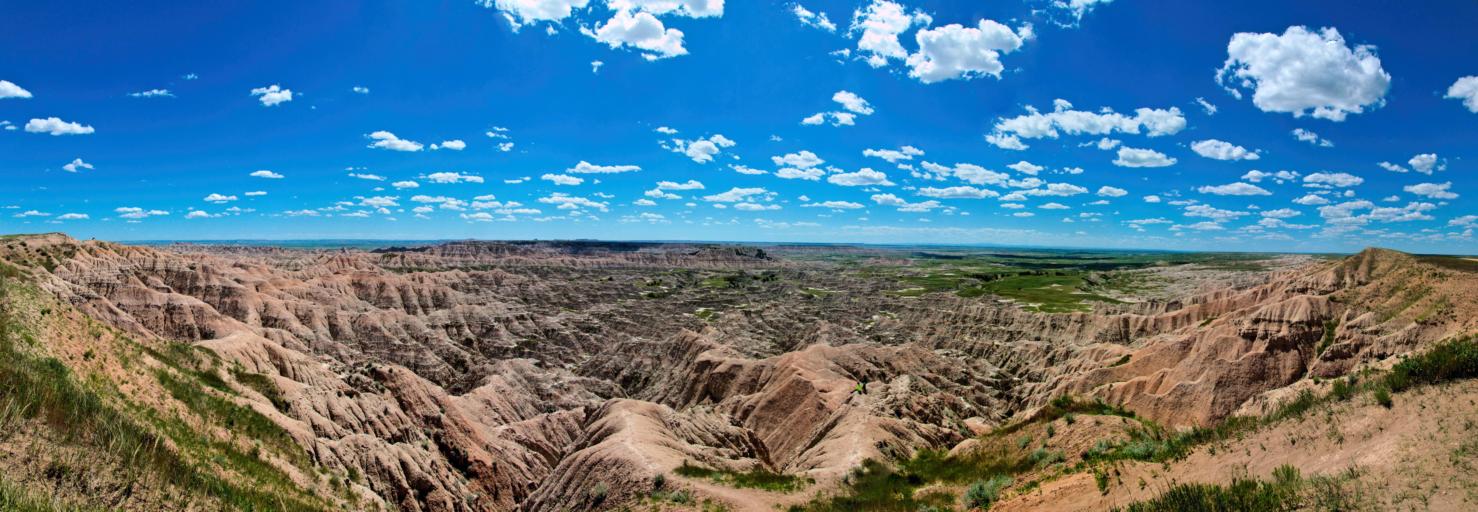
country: US
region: South Dakota
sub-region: Haakon County
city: Philip
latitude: 43.8756
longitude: -102.2561
